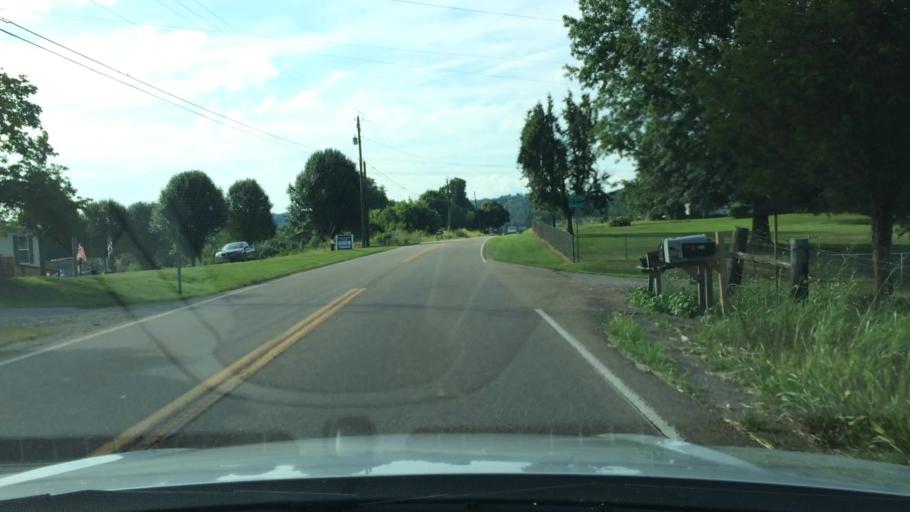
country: US
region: Tennessee
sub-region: Sevier County
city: Seymour
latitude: 35.9244
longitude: -83.6491
